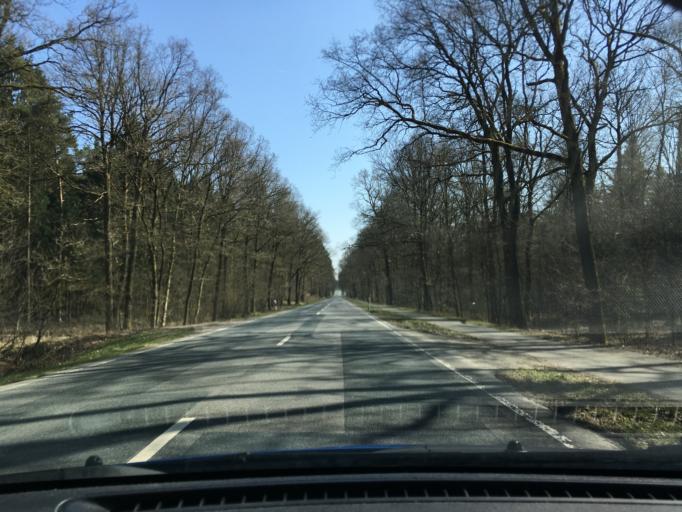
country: DE
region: Lower Saxony
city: Rehlingen
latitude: 53.0905
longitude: 10.2675
